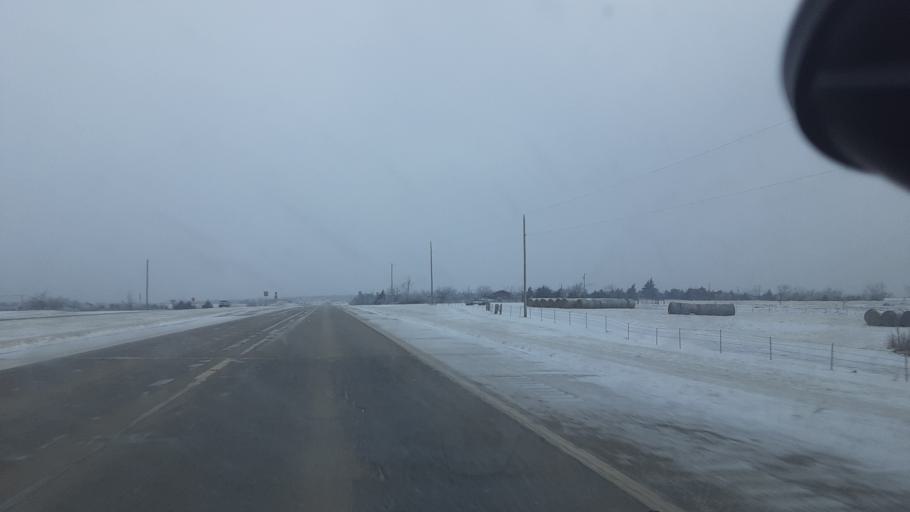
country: US
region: Oklahoma
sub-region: Logan County
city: Langston
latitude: 35.9144
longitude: -97.3306
